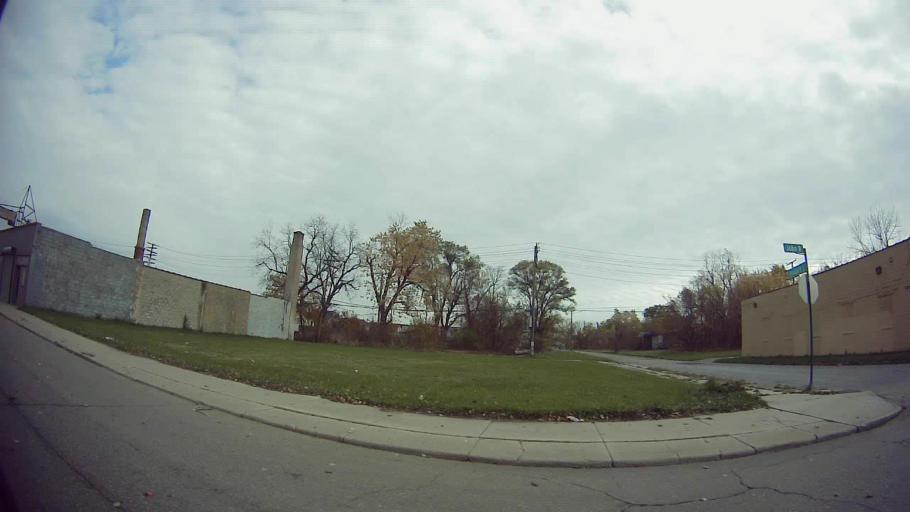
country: US
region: Michigan
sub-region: Wayne County
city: Highland Park
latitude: 42.4284
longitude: -83.1022
